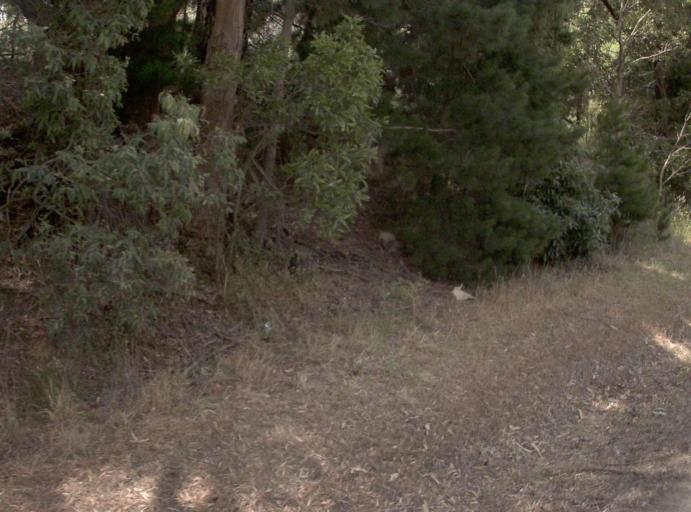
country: AU
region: Victoria
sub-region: Latrobe
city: Traralgon
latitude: -38.2980
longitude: 146.7035
